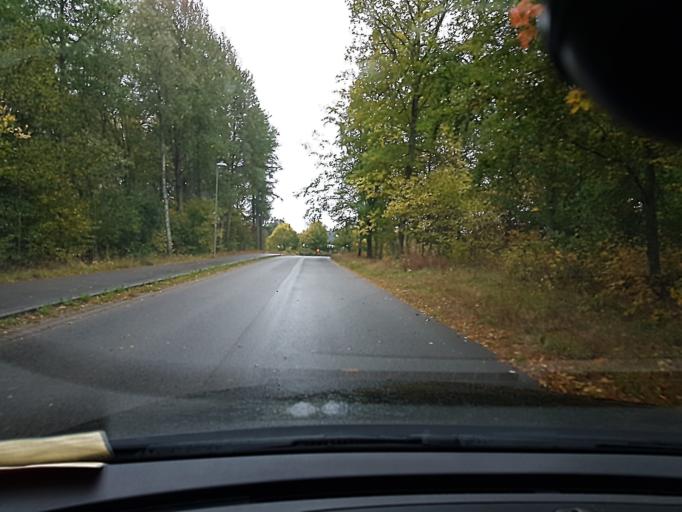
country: SE
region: Kronoberg
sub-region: Vaxjo Kommun
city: Vaexjoe
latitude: 56.8595
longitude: 14.8160
